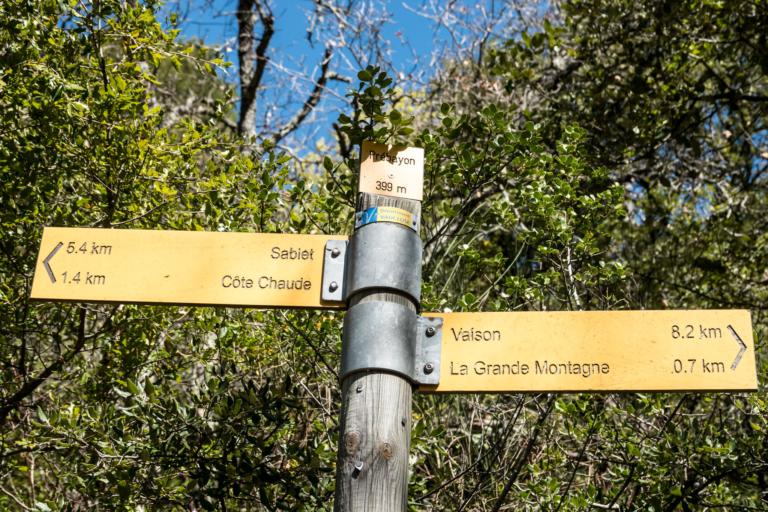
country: FR
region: Provence-Alpes-Cote d'Azur
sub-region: Departement du Vaucluse
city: Sablet
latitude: 44.1923
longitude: 5.0555
